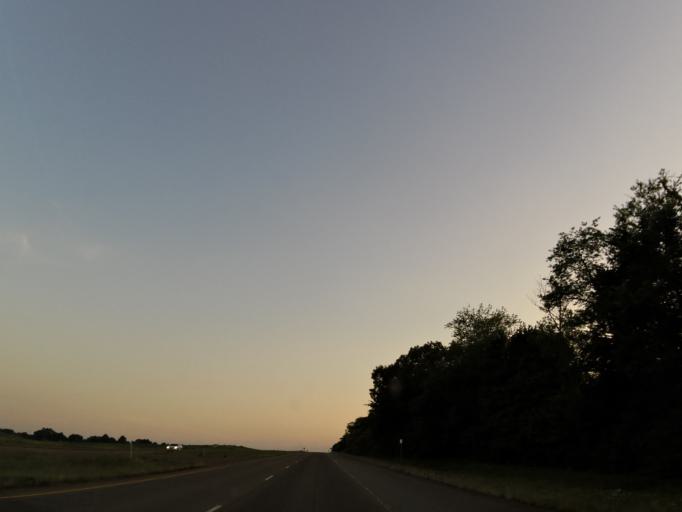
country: US
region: Tennessee
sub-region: Carroll County
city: McKenzie
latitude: 36.1534
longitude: -88.4697
